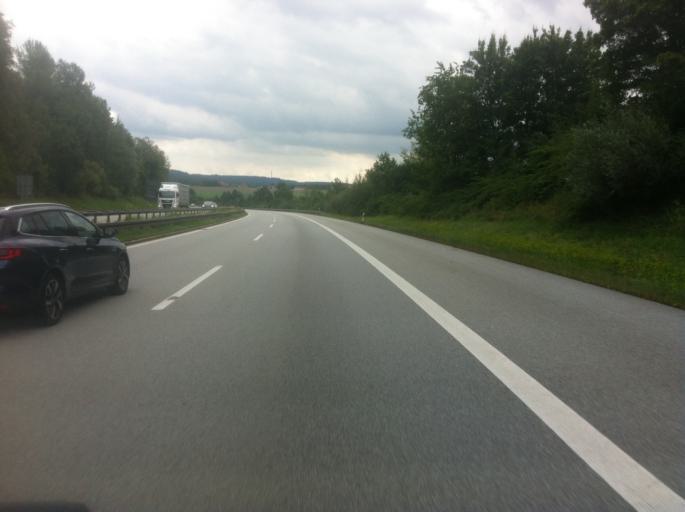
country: DE
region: Bavaria
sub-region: Lower Bavaria
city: Tiefenbach
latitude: 48.5775
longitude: 13.3650
